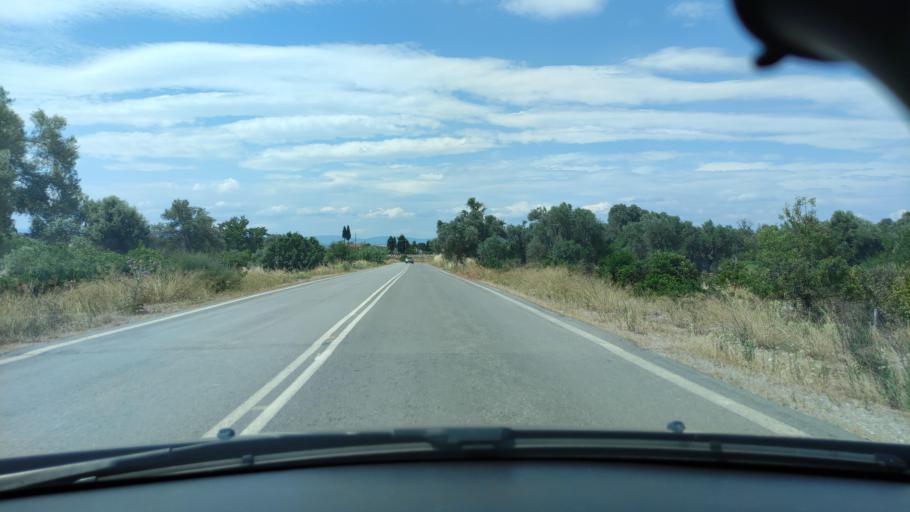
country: GR
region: Central Greece
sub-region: Nomos Evvoias
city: Filla
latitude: 38.4424
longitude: 23.6710
